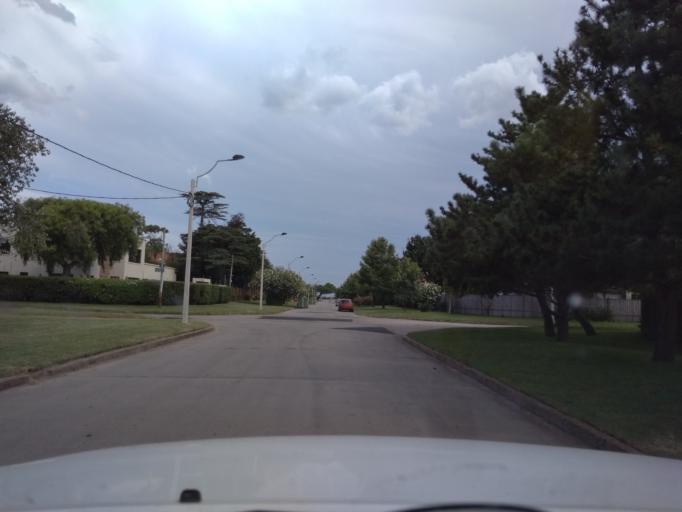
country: UY
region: Canelones
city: Barra de Carrasco
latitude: -34.8841
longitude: -56.0485
